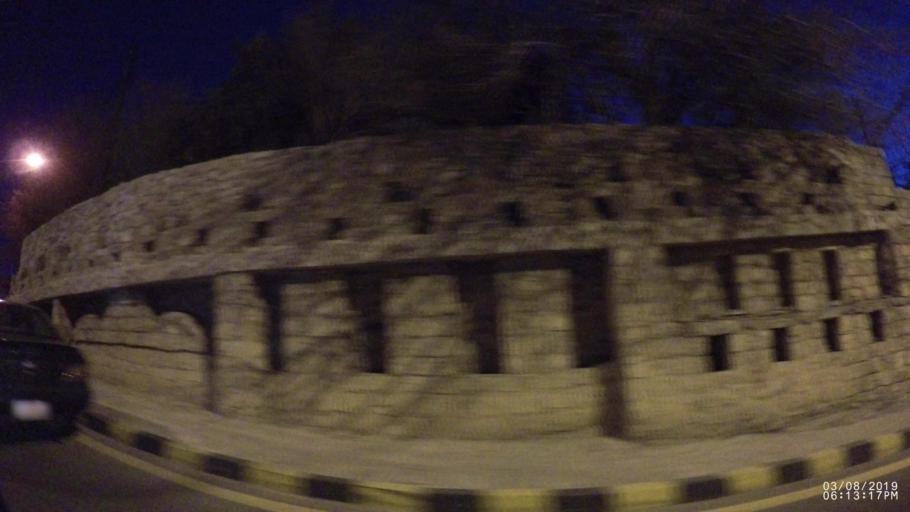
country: JO
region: Ma'an
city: Petra
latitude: 30.3246
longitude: 35.4975
